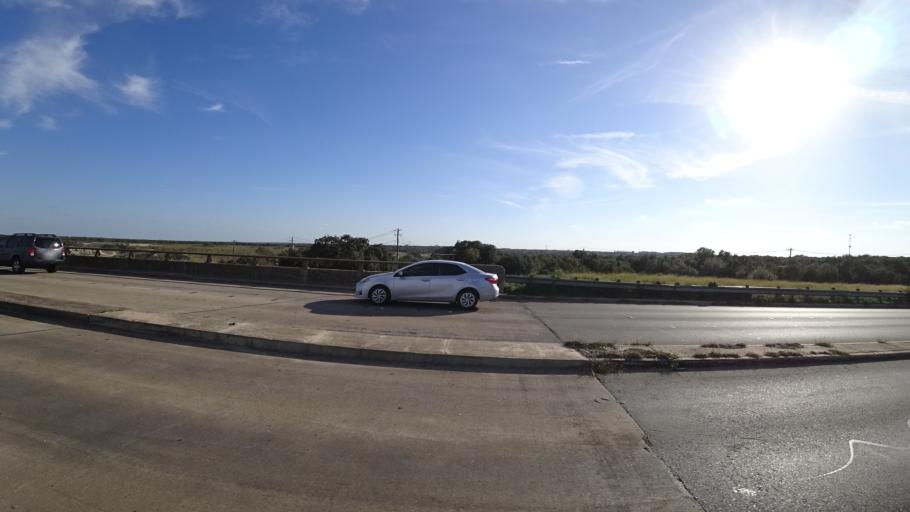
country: US
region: Texas
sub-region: Travis County
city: Wells Branch
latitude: 30.4495
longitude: -97.7231
